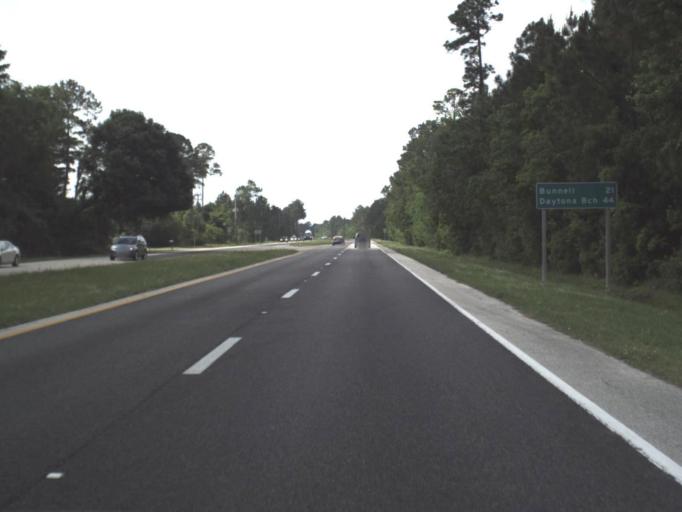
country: US
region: Florida
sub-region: Saint Johns County
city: Saint Augustine Shores
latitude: 29.7552
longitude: -81.3128
